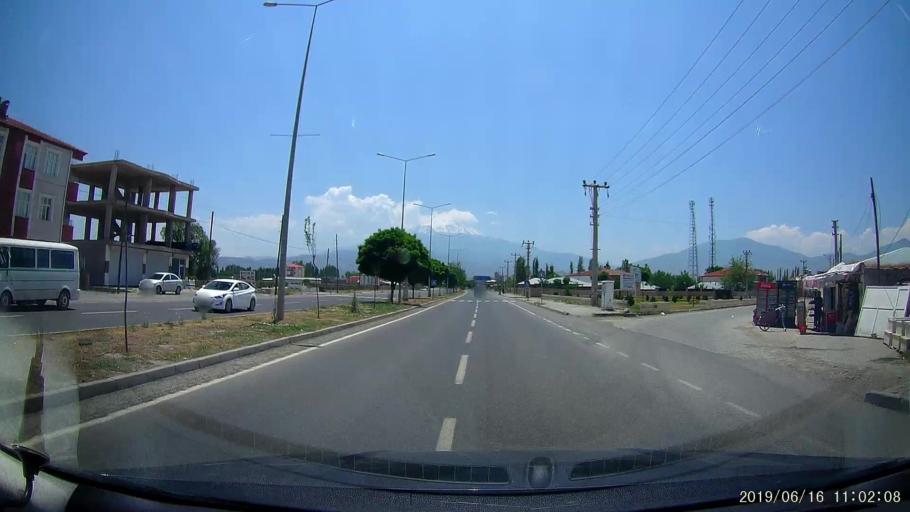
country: TR
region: Igdir
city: Igdir
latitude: 39.9093
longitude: 44.0569
